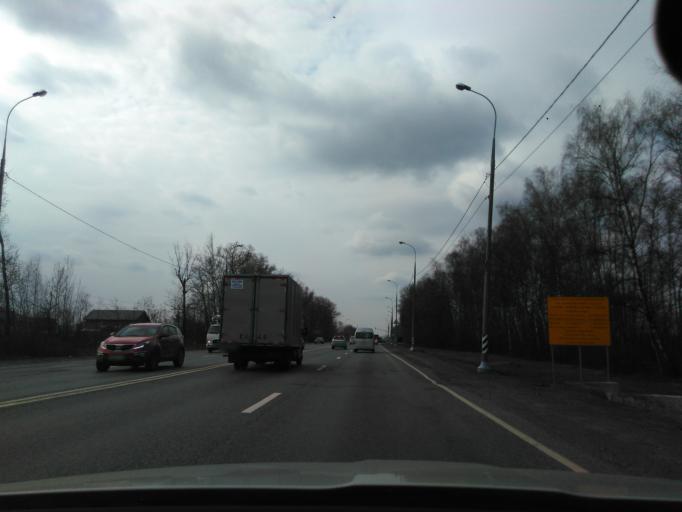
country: RU
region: Moskovskaya
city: Sheremet'yevskiy
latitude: 56.0010
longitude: 37.5380
